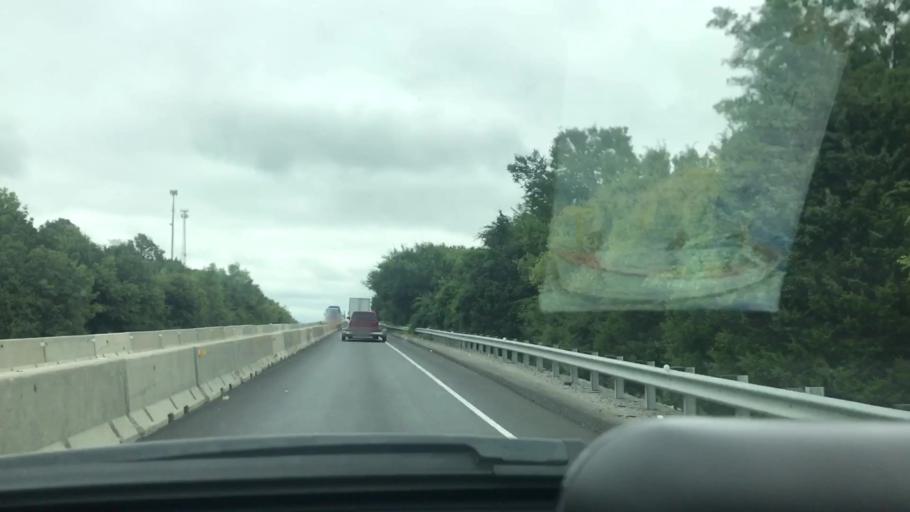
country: US
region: Oklahoma
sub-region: McIntosh County
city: Eufaula
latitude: 35.2851
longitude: -95.5931
